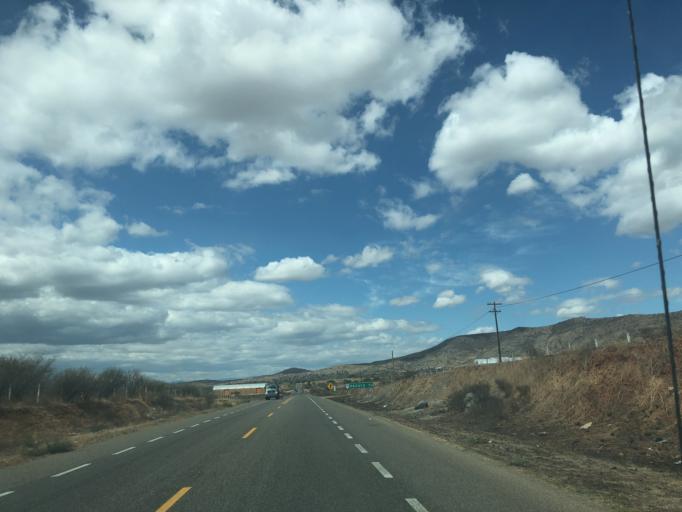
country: MX
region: Oaxaca
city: San Martin de los Canseco
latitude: 16.6362
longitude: -96.7387
